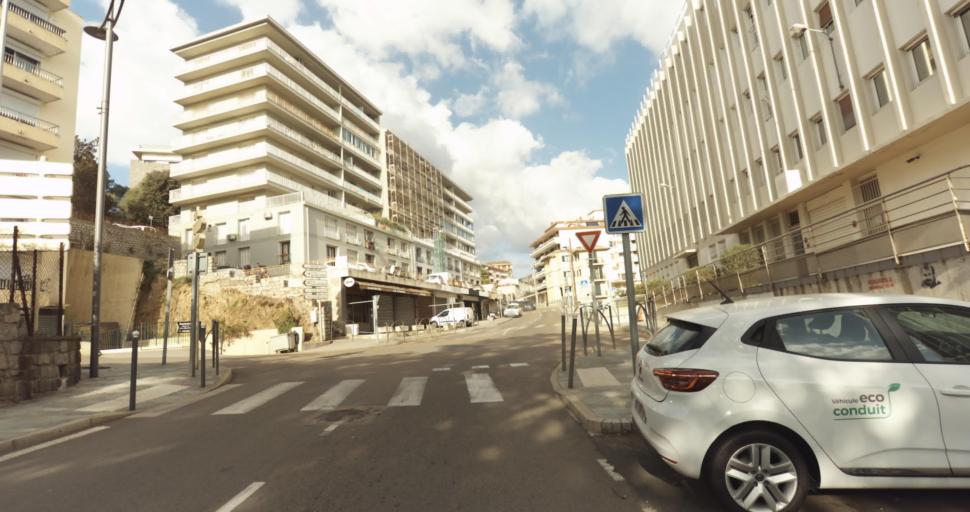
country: FR
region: Corsica
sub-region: Departement de la Corse-du-Sud
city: Ajaccio
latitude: 41.9284
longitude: 8.7350
